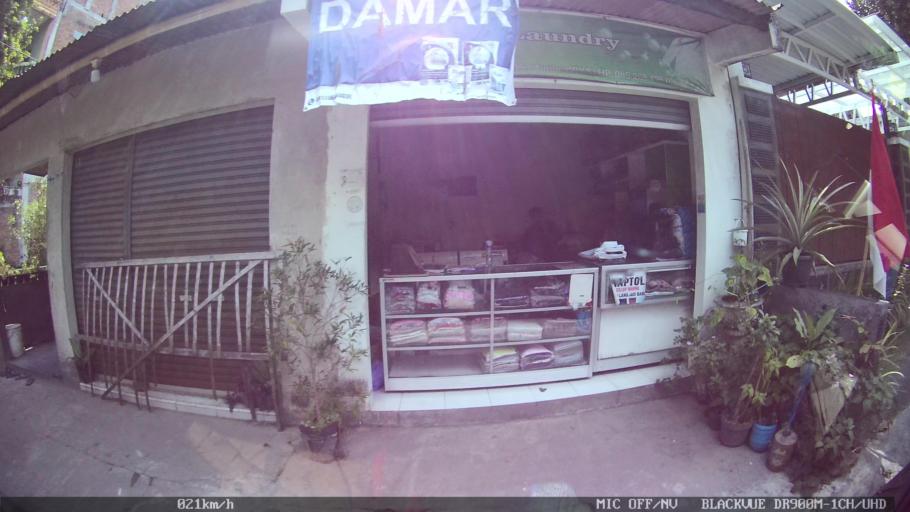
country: ID
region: Daerah Istimewa Yogyakarta
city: Gamping Lor
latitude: -7.8083
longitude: 110.3440
